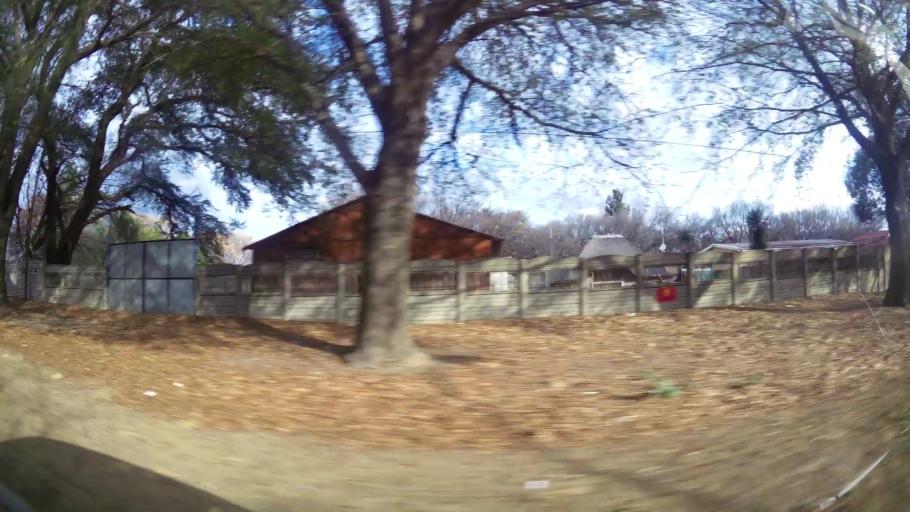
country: ZA
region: Orange Free State
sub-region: Fezile Dabi District Municipality
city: Sasolburg
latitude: -26.8045
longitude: 27.8142
